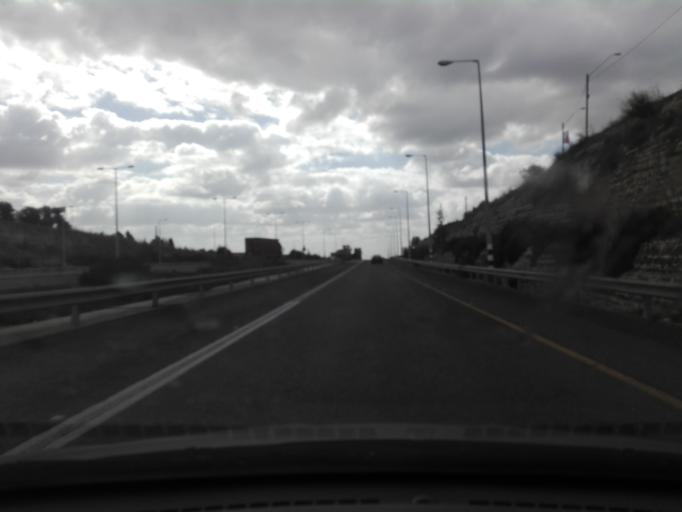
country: IL
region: Haifa
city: Daliyat el Karmil
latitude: 32.6338
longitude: 35.0637
